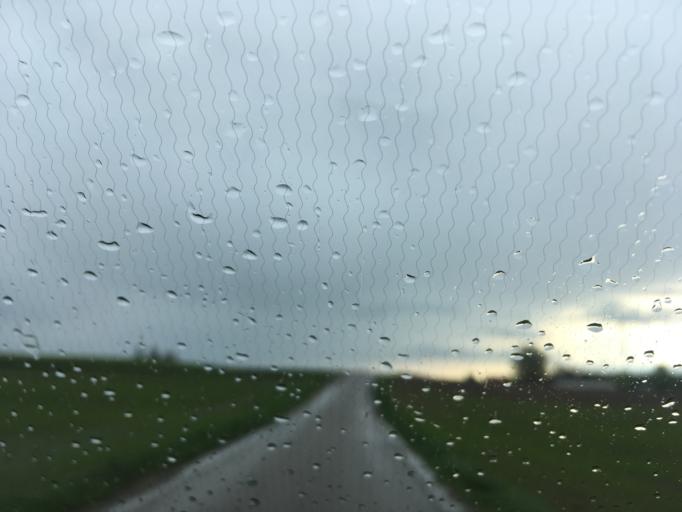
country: PL
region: Warmian-Masurian Voivodeship
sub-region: Powiat dzialdowski
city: Rybno
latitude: 53.3835
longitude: 19.9730
